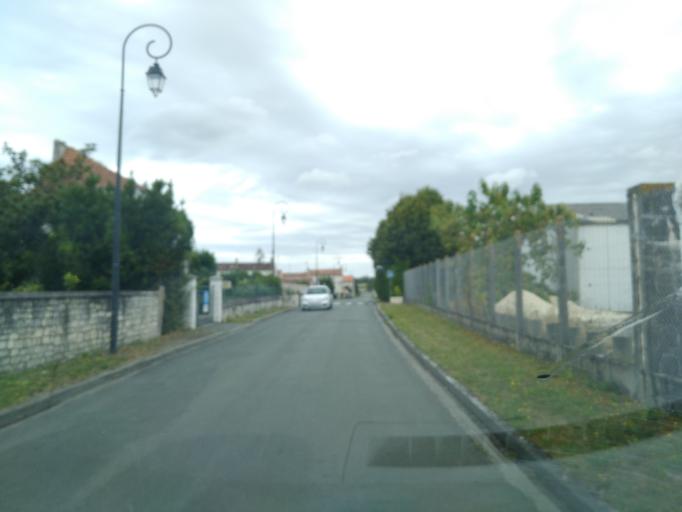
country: FR
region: Poitou-Charentes
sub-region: Departement de la Charente-Maritime
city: Pons
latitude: 45.5971
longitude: -0.5157
